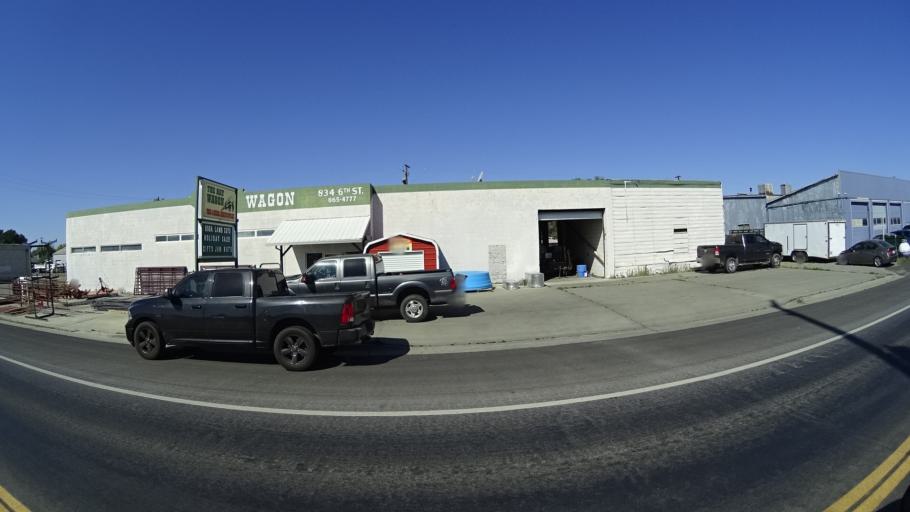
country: US
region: California
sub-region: Glenn County
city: Orland
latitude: 39.7455
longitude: -122.1975
